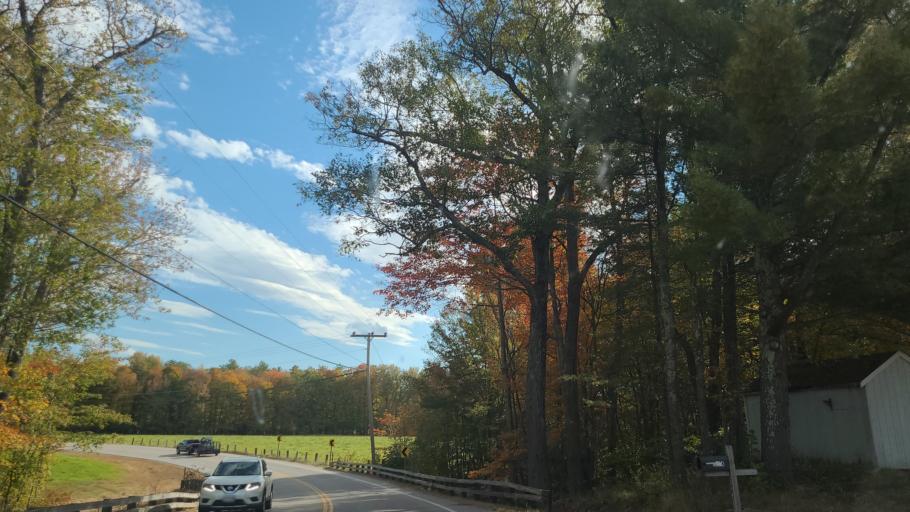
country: US
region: New Hampshire
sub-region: Carroll County
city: Conway
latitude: 43.9880
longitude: -71.1235
